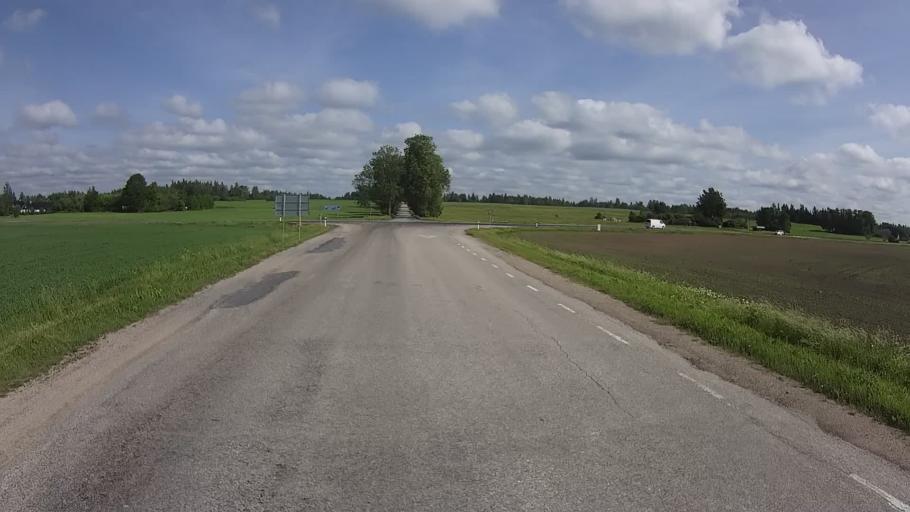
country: EE
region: Vorumaa
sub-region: Antsla vald
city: Vana-Antsla
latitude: 57.8689
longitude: 26.6086
